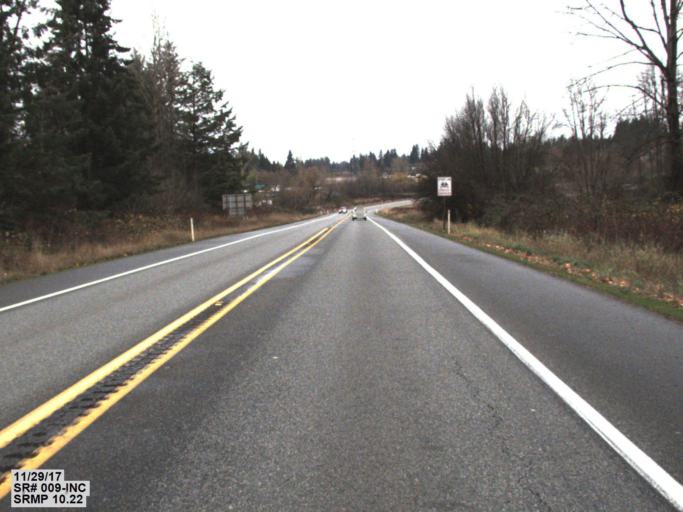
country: US
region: Washington
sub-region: Snohomish County
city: Snohomish
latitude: 47.9249
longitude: -122.1082
